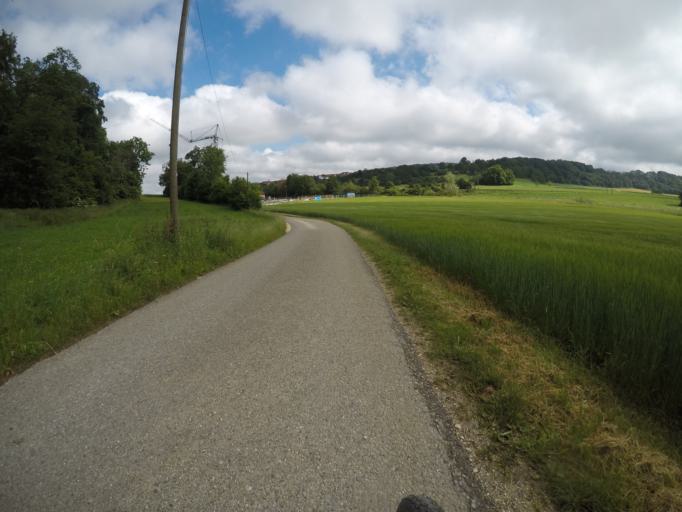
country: DE
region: Baden-Wuerttemberg
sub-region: Tuebingen Region
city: Lonsee
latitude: 48.5288
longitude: 9.9310
